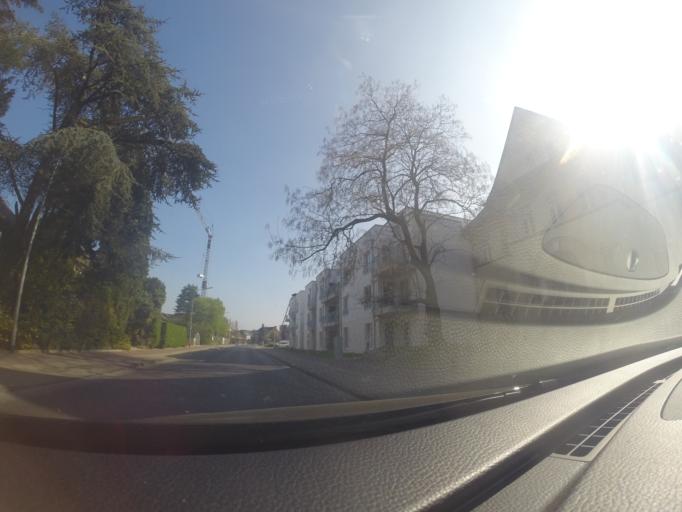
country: DE
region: North Rhine-Westphalia
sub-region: Regierungsbezirk Dusseldorf
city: Xanten
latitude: 51.6600
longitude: 6.4512
